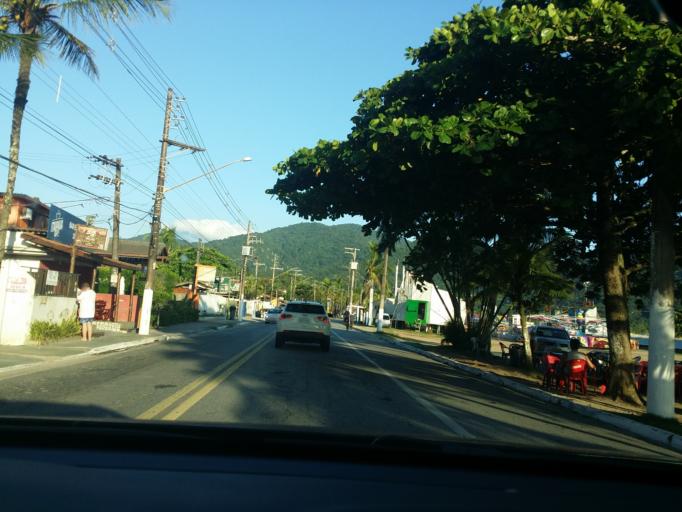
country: BR
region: Sao Paulo
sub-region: Sao Sebastiao
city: Sao Sebastiao
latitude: -23.7831
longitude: -45.6322
